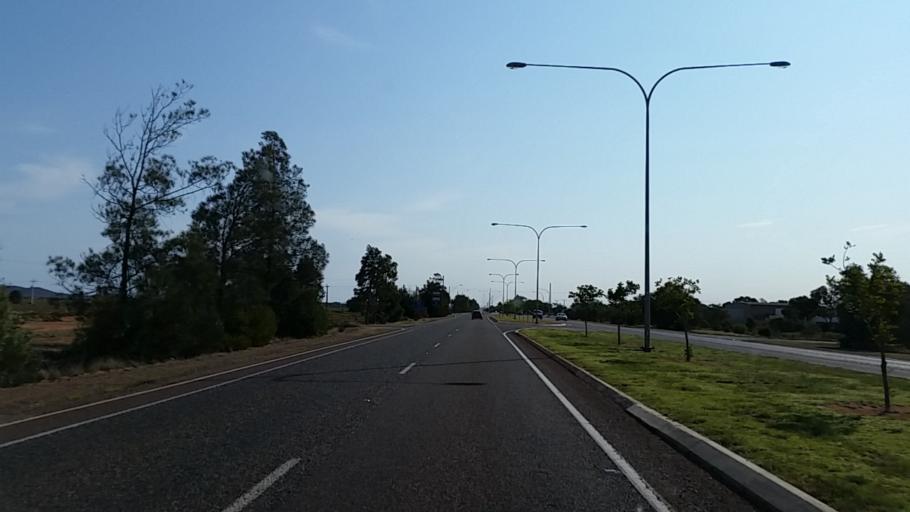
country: AU
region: South Australia
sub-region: Whyalla
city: Whyalla
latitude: -33.0417
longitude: 137.5470
